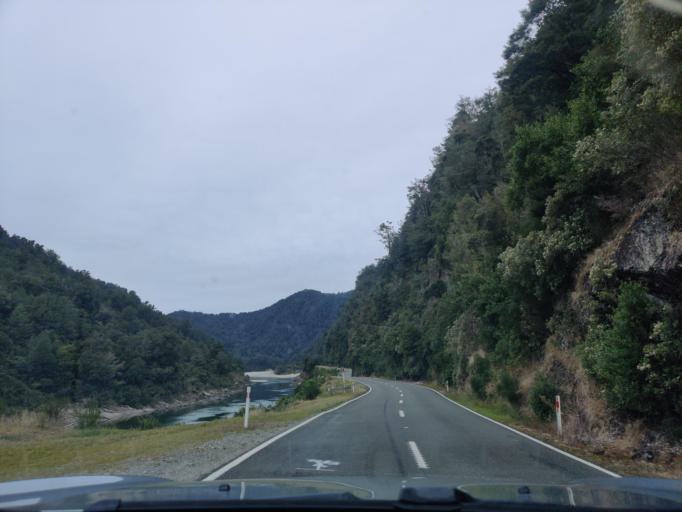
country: NZ
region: West Coast
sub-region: Buller District
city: Westport
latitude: -41.8576
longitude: 171.7609
